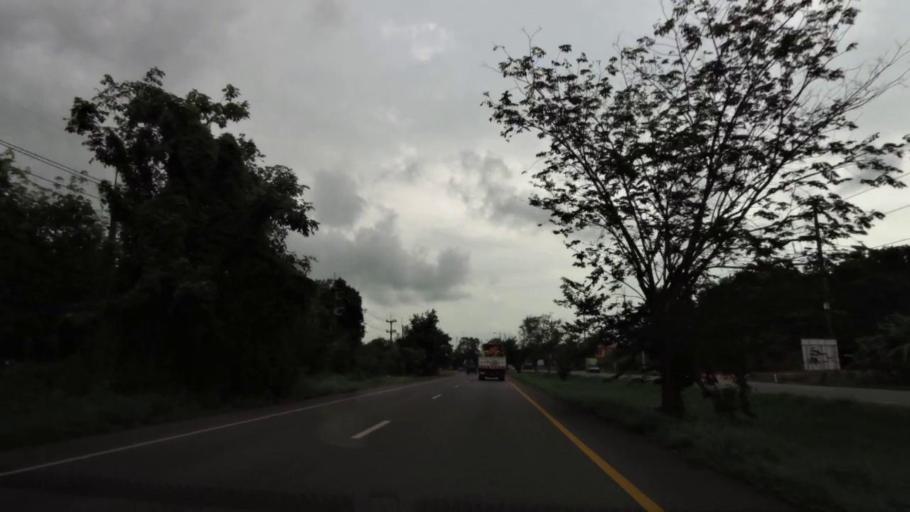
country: TH
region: Chanthaburi
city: Tha Mai
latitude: 12.7128
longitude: 101.9808
